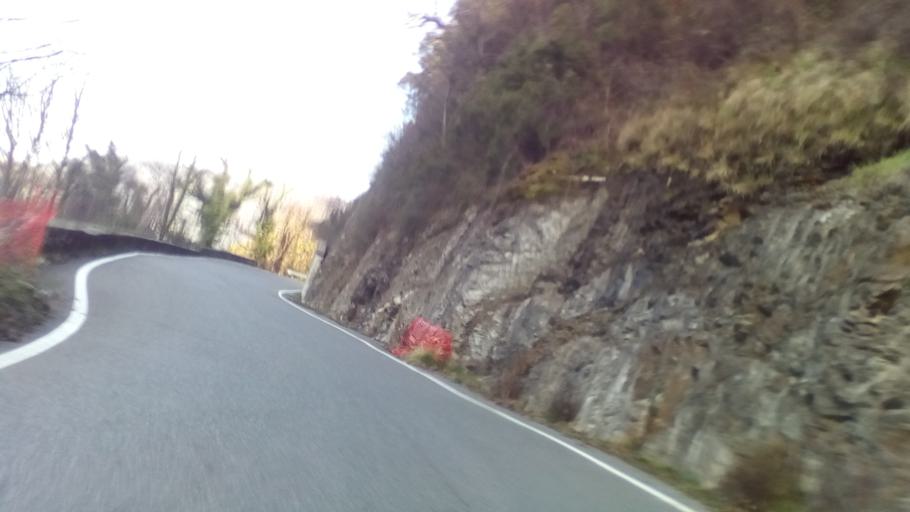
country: IT
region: Tuscany
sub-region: Provincia di Massa-Carrara
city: Montignoso
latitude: 44.0532
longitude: 10.1904
